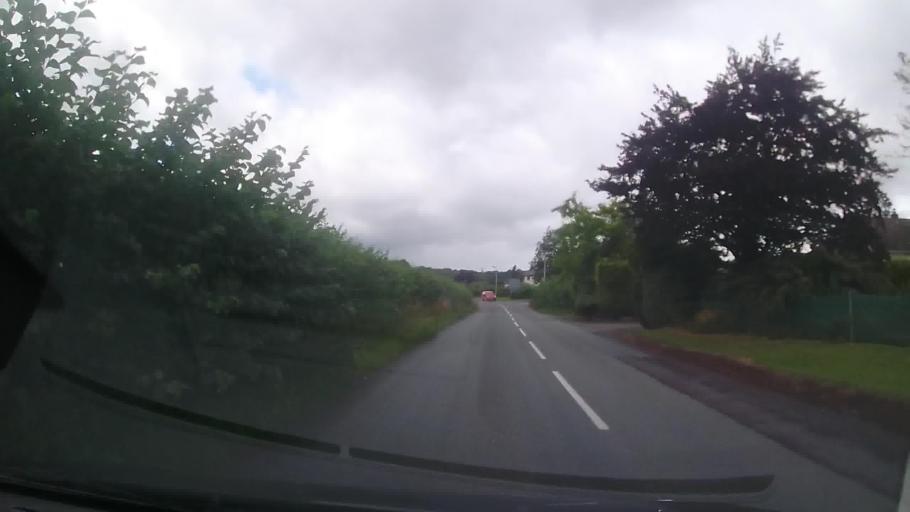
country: GB
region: England
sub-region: Shropshire
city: Craven Arms
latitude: 52.4391
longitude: -2.8474
